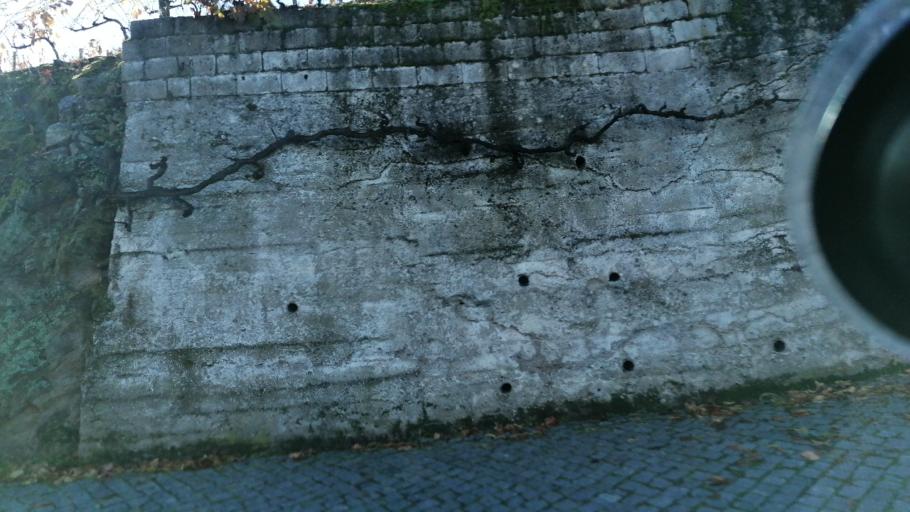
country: PT
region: Viseu
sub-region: Lamego
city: Lamego
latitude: 41.1093
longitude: -7.7899
